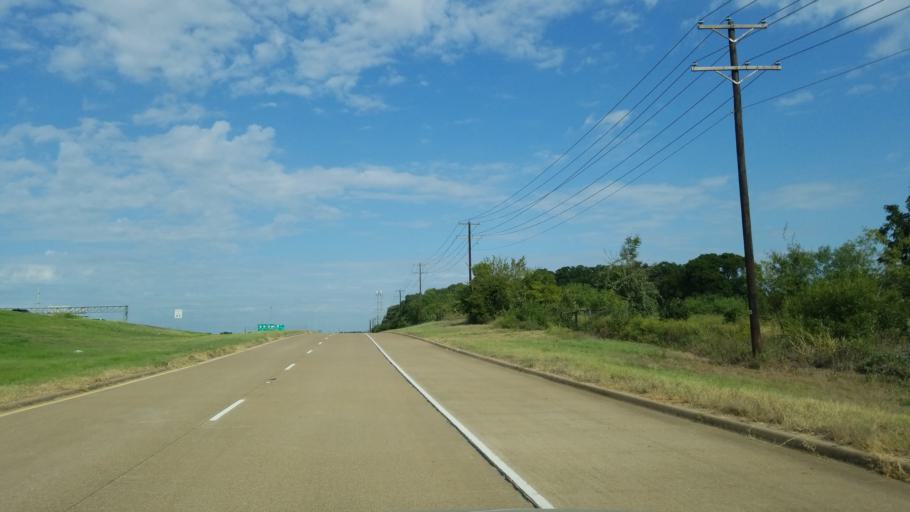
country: US
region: Texas
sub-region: Tarrant County
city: Grapevine
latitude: 32.8968
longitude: -97.0873
